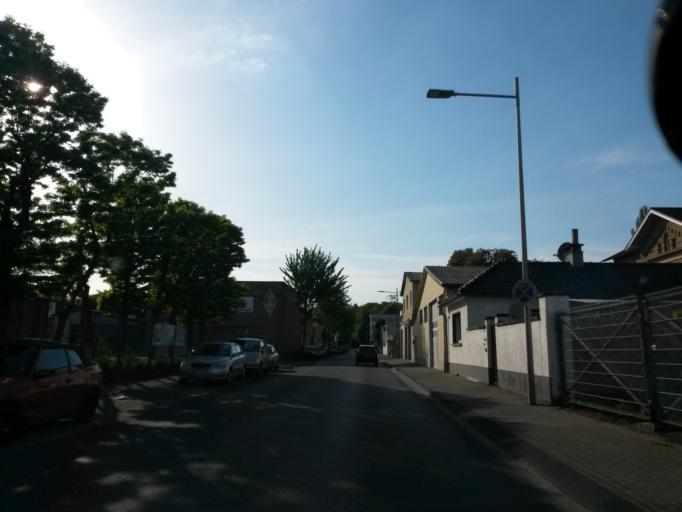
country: DE
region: North Rhine-Westphalia
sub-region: Regierungsbezirk Koln
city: Siegburg
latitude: 50.8005
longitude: 7.1988
